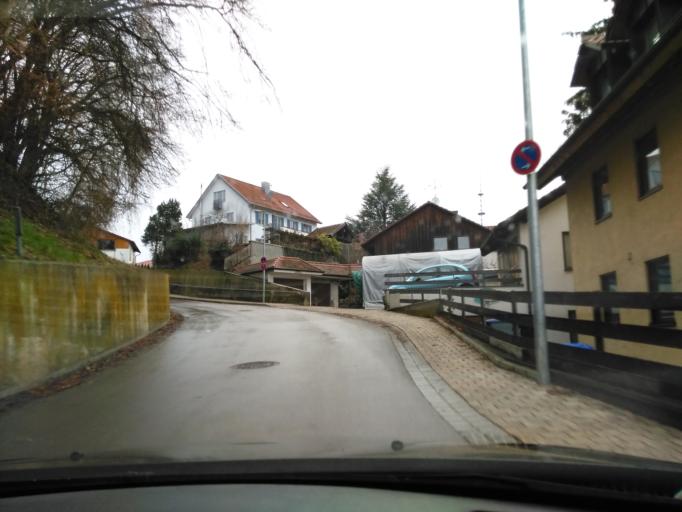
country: DE
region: Bavaria
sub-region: Upper Bavaria
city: Fuerstenfeldbruck
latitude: 48.1859
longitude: 11.2211
